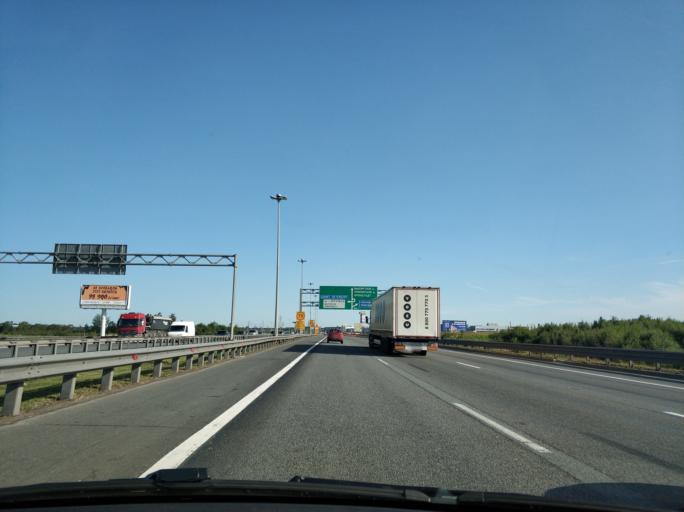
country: RU
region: Leningrad
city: Bugry
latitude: 60.0801
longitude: 30.3799
